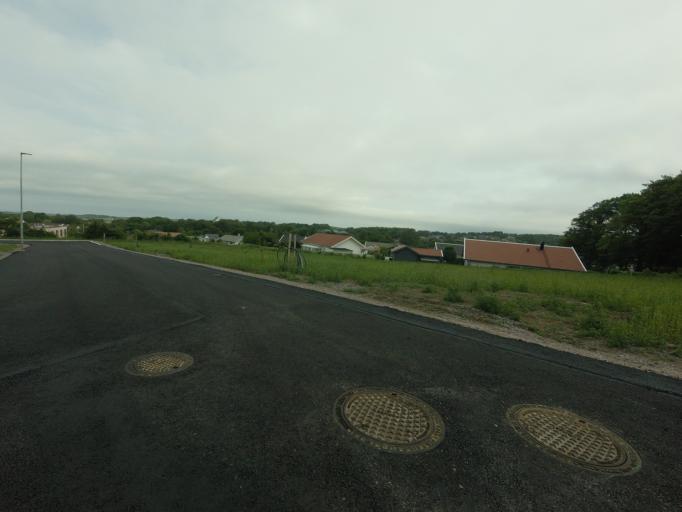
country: SE
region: Skane
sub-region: Bastads Kommun
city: Forslov
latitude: 56.3498
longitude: 12.8255
